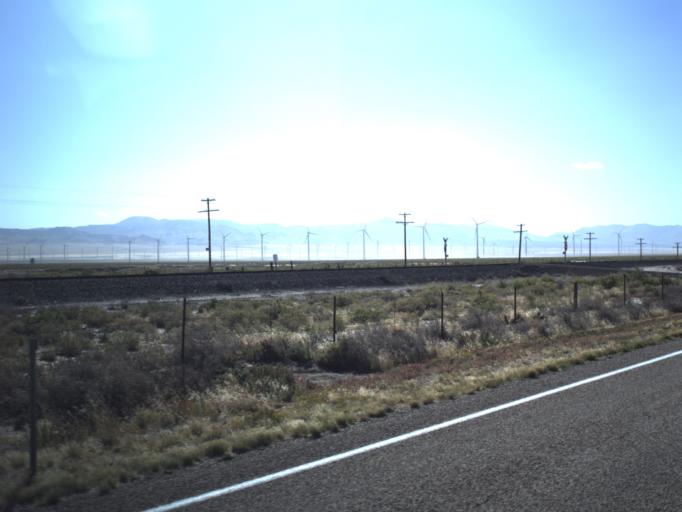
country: US
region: Utah
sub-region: Beaver County
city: Milford
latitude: 38.6105
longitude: -112.9861
